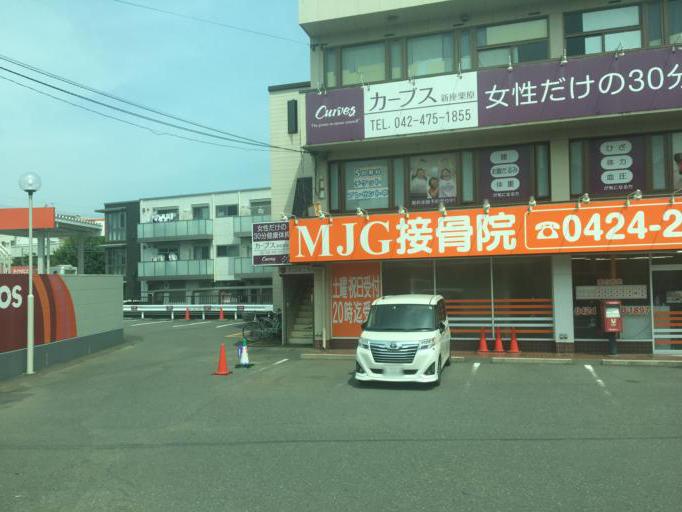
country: JP
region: Tokyo
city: Tanashicho
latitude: 35.7630
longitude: 139.5524
